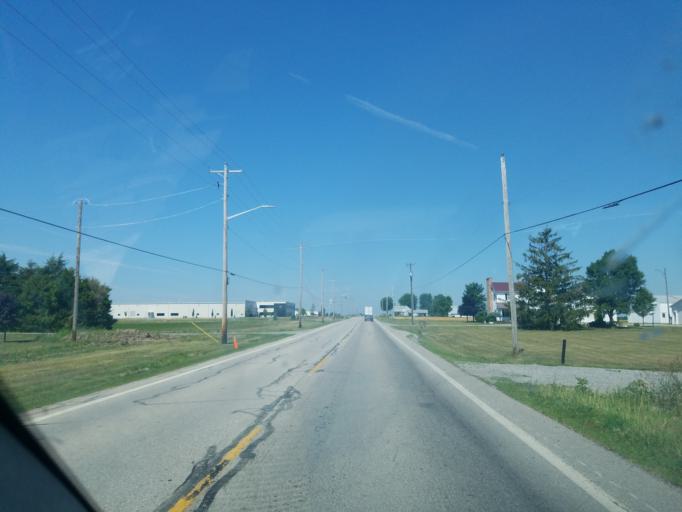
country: US
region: Ohio
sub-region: Shelby County
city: Jackson Center
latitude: 40.4398
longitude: -84.0531
